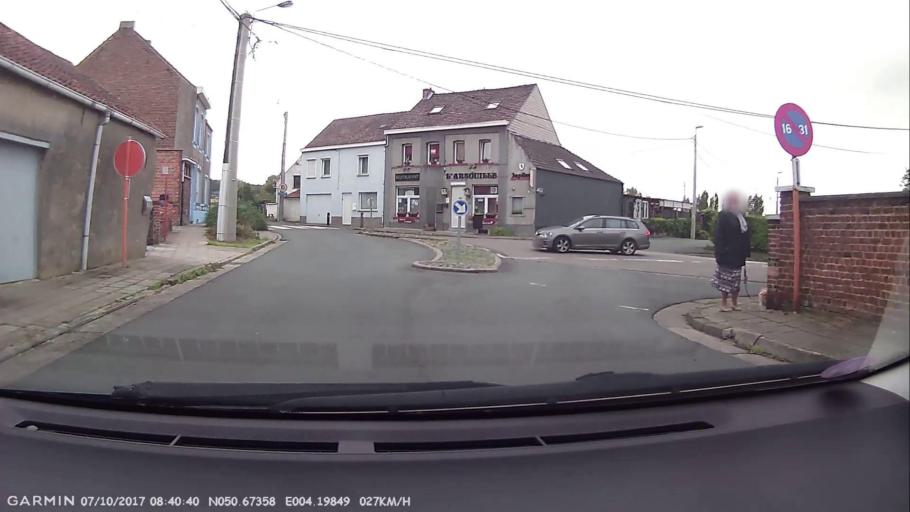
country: BE
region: Wallonia
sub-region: Province du Brabant Wallon
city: Tubize
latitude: 50.6736
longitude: 4.1985
